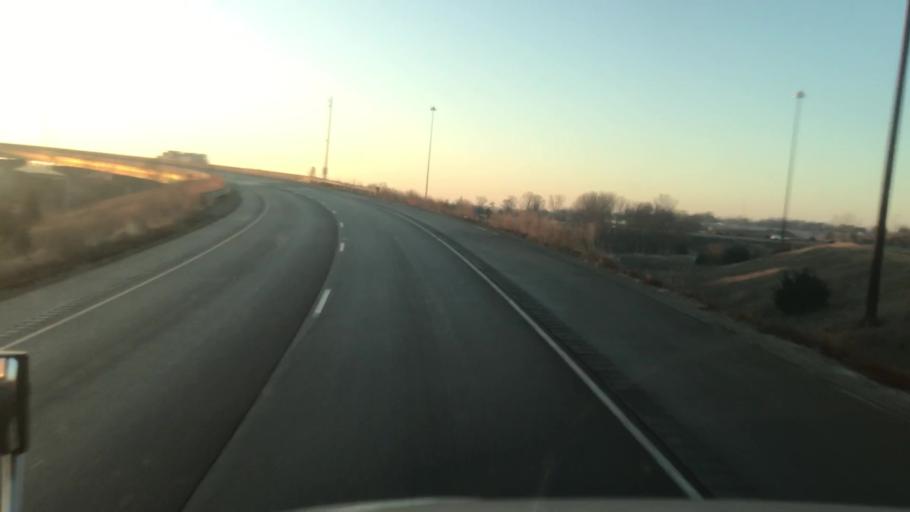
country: US
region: Iowa
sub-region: Black Hawk County
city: Evansdale
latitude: 42.4566
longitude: -92.3147
